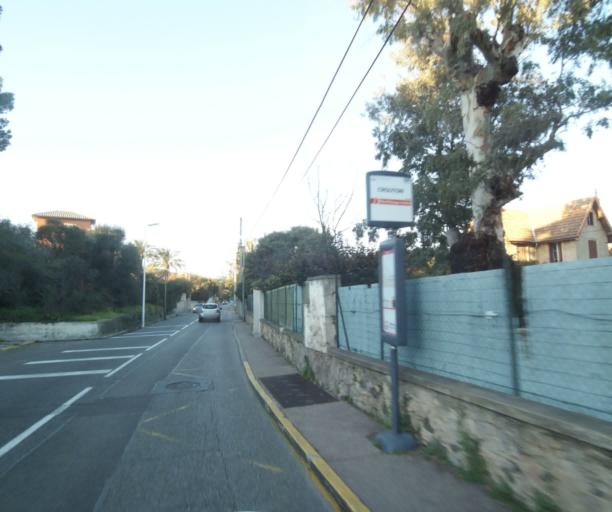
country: FR
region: Provence-Alpes-Cote d'Azur
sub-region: Departement des Alpes-Maritimes
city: Antibes
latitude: 43.5683
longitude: 7.1244
